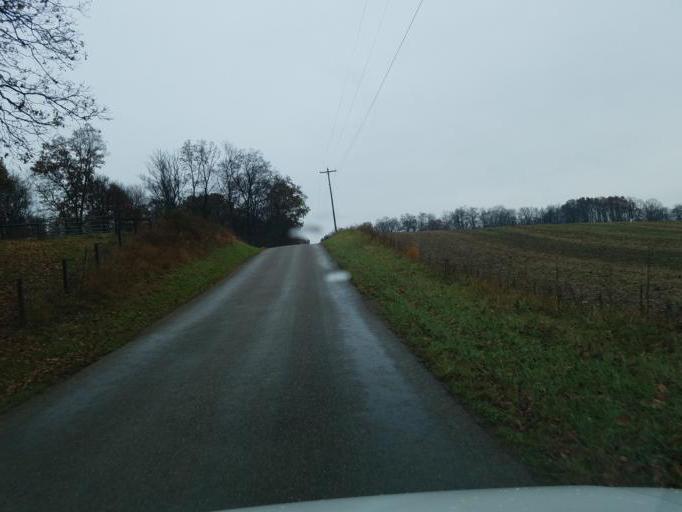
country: US
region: Ohio
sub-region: Knox County
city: Fredericktown
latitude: 40.5574
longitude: -82.5792
